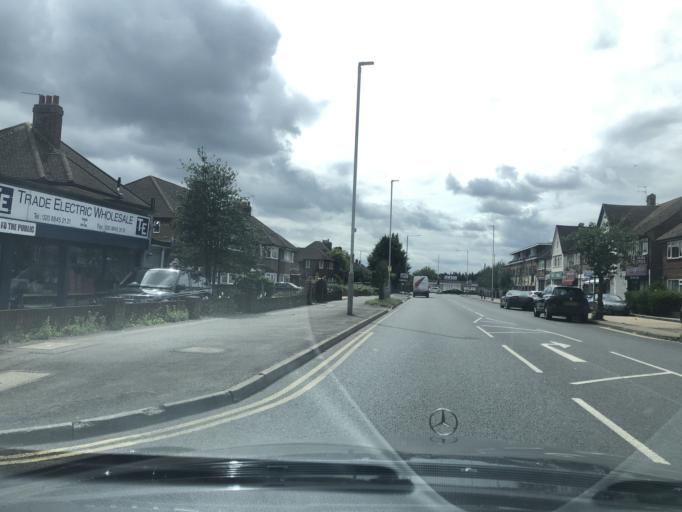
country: GB
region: England
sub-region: Greater London
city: Ruislip
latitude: 51.5547
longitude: -0.4022
